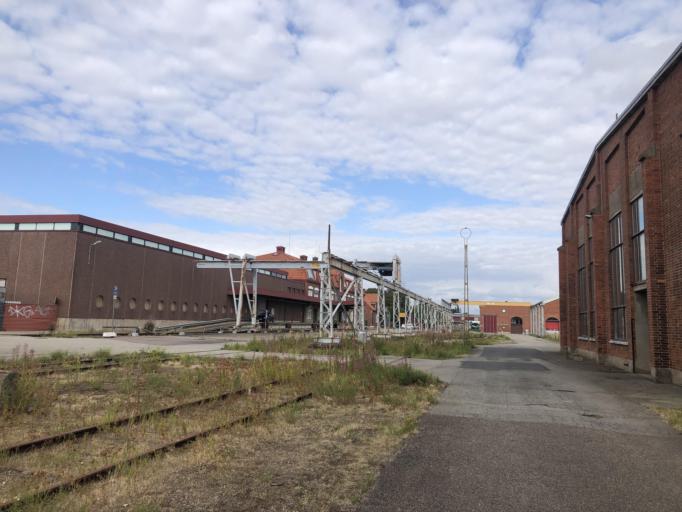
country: SE
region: Skane
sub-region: Malmo
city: Malmoe
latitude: 55.6058
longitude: 13.0407
